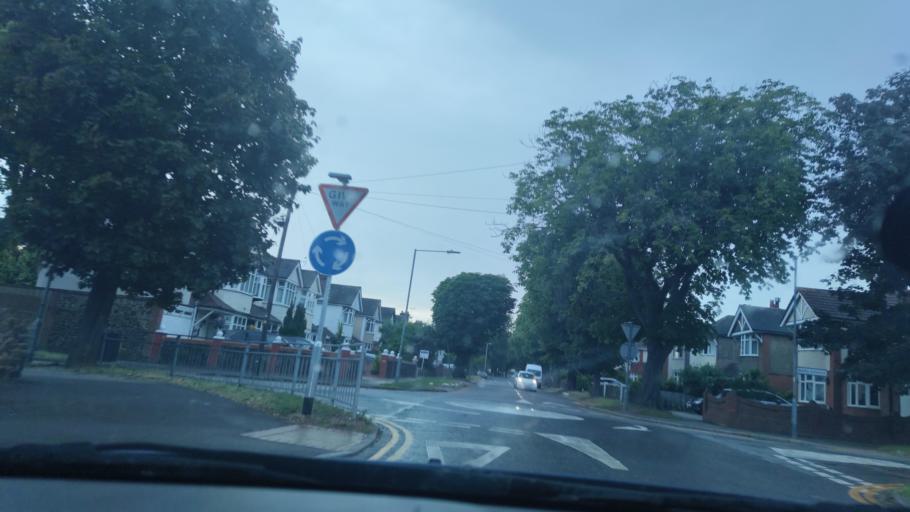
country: GB
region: England
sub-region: Borough of Thurrock
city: Grays
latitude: 51.4865
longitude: 0.3319
